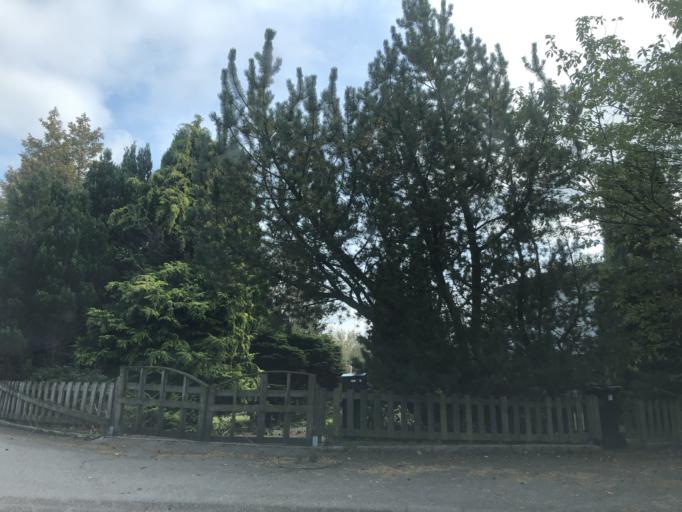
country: SE
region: Vaestra Goetaland
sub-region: Goteborg
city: Majorna
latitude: 57.6529
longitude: 11.8903
